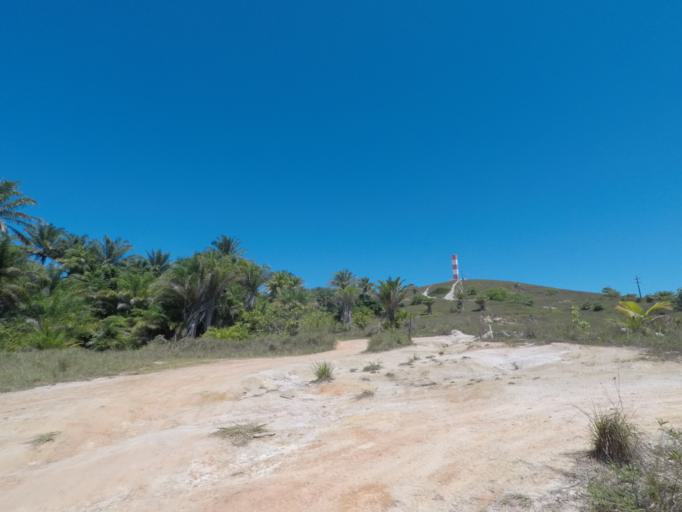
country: BR
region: Bahia
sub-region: Camamu
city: Camamu
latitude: -13.9548
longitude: -38.9455
